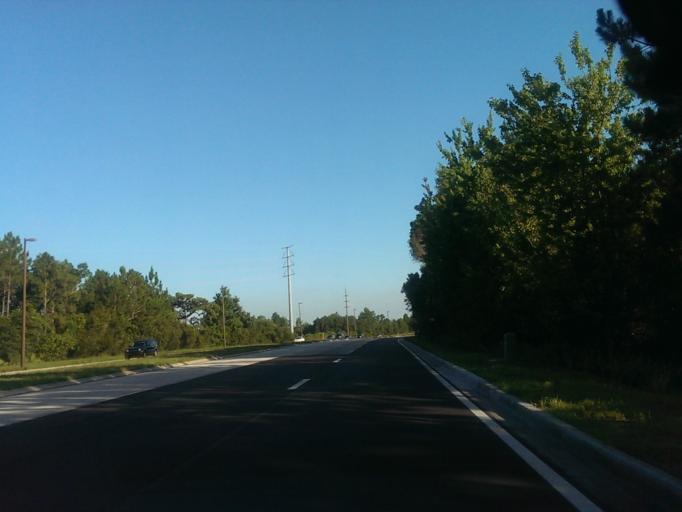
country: US
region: Florida
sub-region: Orange County
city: Williamsburg
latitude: 28.3731
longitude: -81.4870
